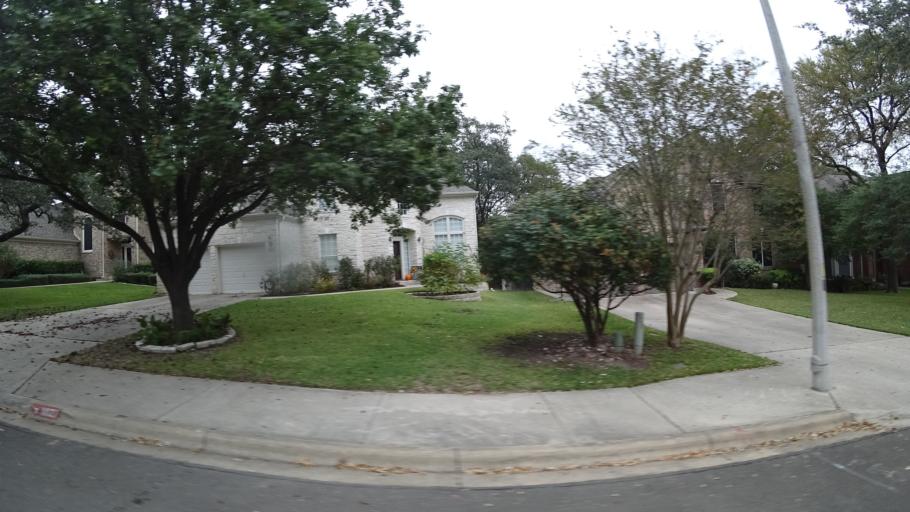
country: US
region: Texas
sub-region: Williamson County
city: Anderson Mill
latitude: 30.4354
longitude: -97.8294
